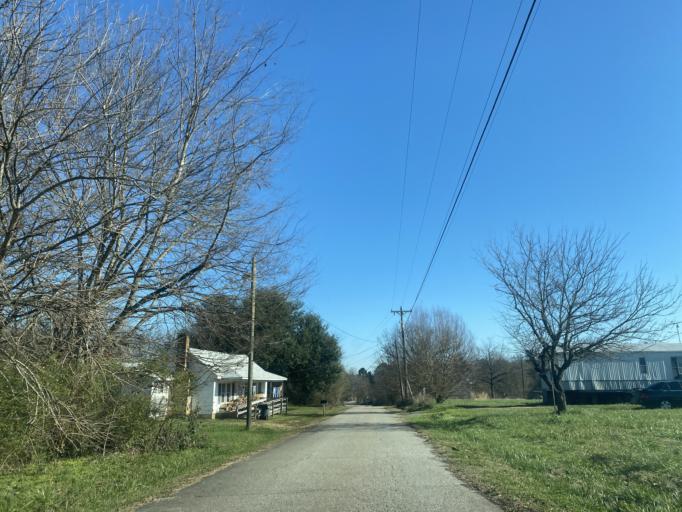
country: US
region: South Carolina
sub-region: Spartanburg County
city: Mayo
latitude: 35.1329
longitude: -81.7883
